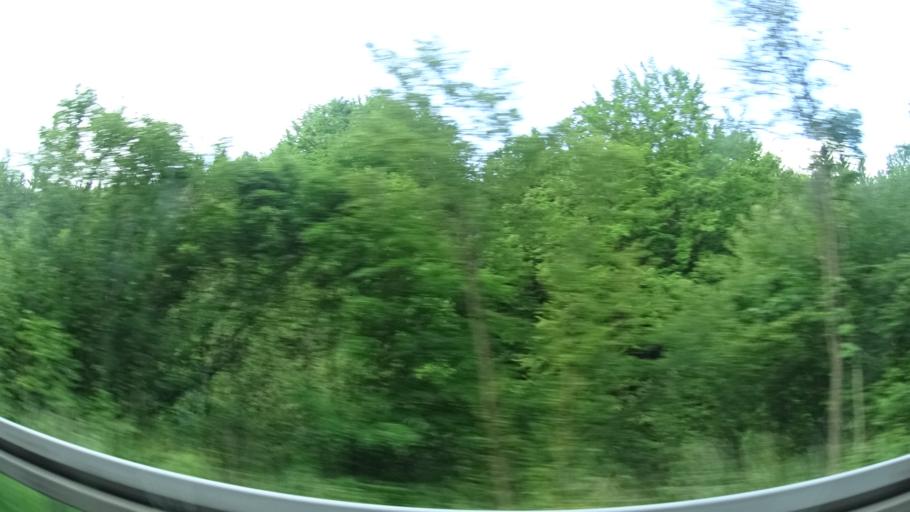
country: DE
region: Bavaria
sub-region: Regierungsbezirk Unterfranken
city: Rechtenbach
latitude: 49.9721
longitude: 9.5248
